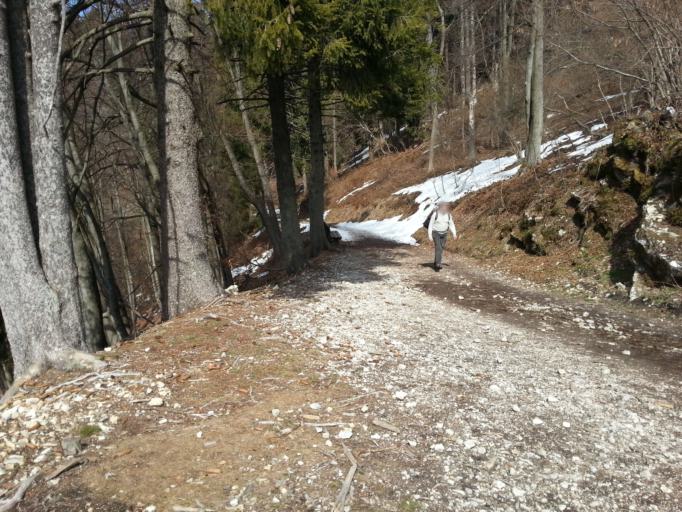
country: IT
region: Lombardy
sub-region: Provincia di Varese
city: Castello Cabiaglio
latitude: 45.8676
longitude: 8.7572
